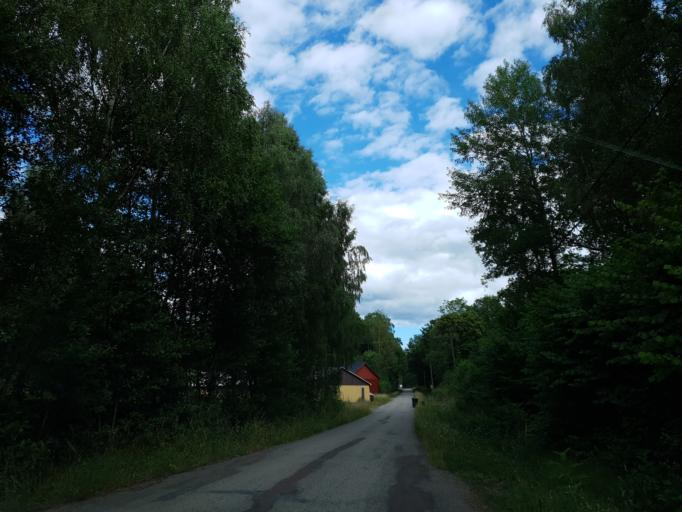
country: SE
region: Kalmar
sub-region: Emmaboda Kommun
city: Emmaboda
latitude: 56.6230
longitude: 15.6646
